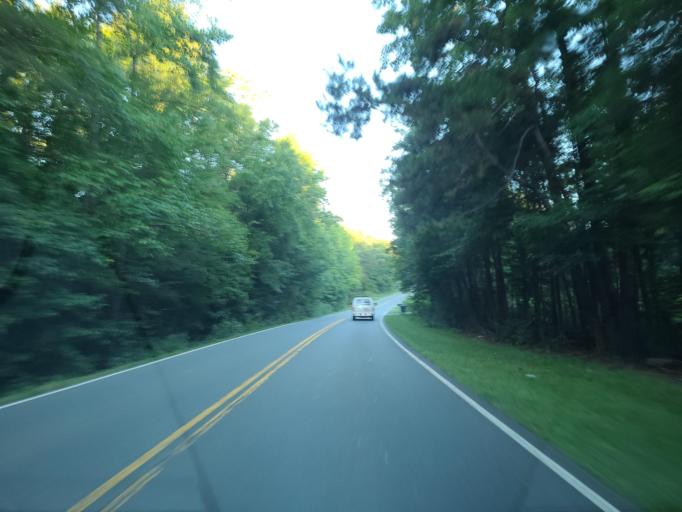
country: US
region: North Carolina
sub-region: Union County
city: Weddington
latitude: 35.0166
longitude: -80.7523
